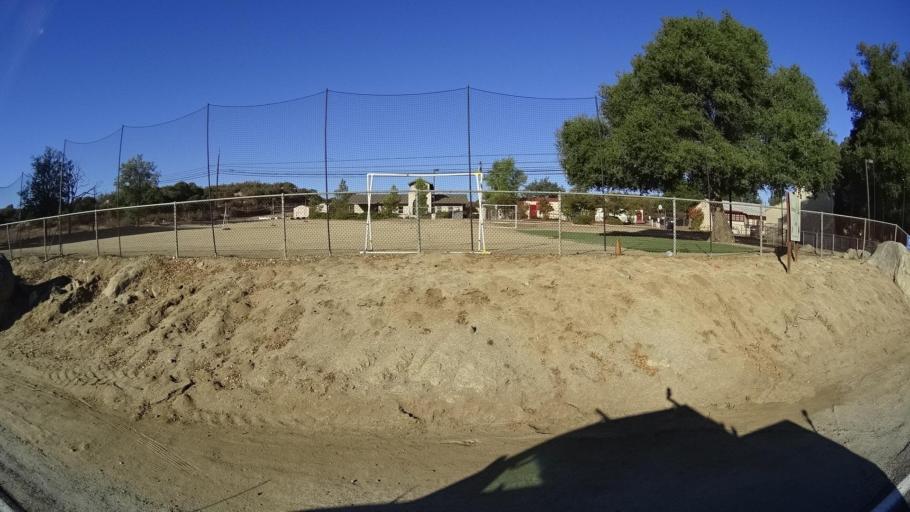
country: US
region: California
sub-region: San Diego County
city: Campo
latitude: 32.6246
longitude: -116.4746
